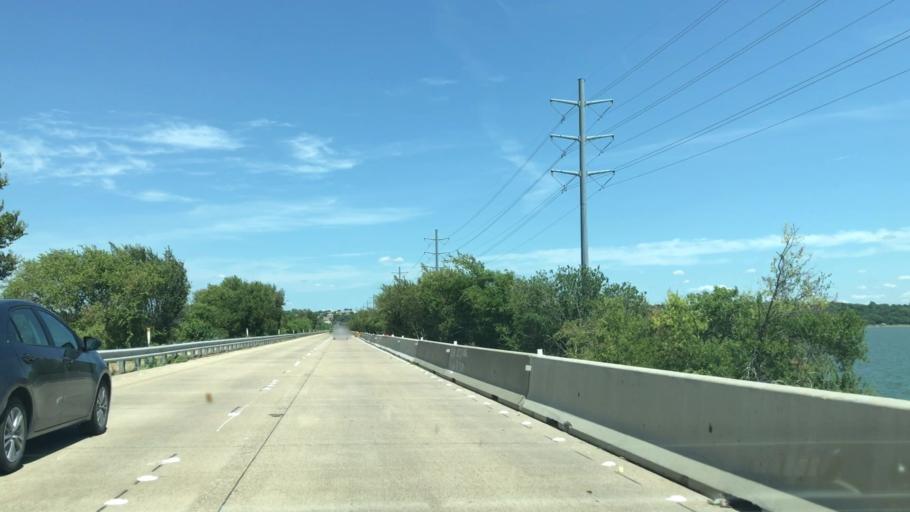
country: US
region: Texas
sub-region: Rockwall County
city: Rockwall
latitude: 32.9257
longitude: -96.4869
